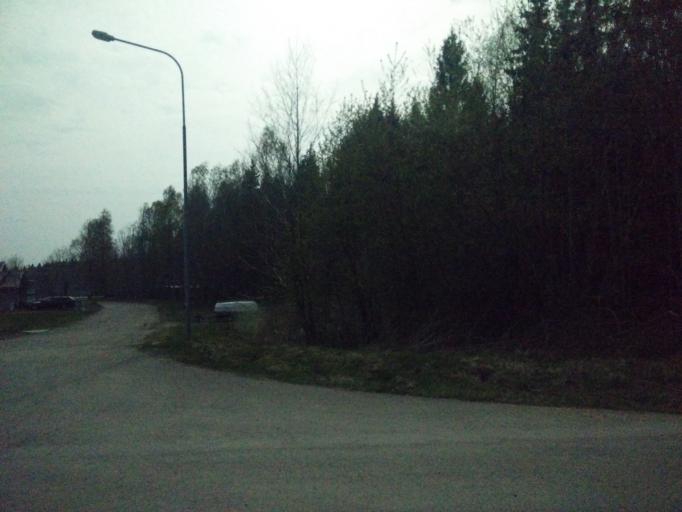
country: SE
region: Vaermland
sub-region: Munkfors Kommun
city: Munkfors
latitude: 59.8355
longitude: 13.5113
